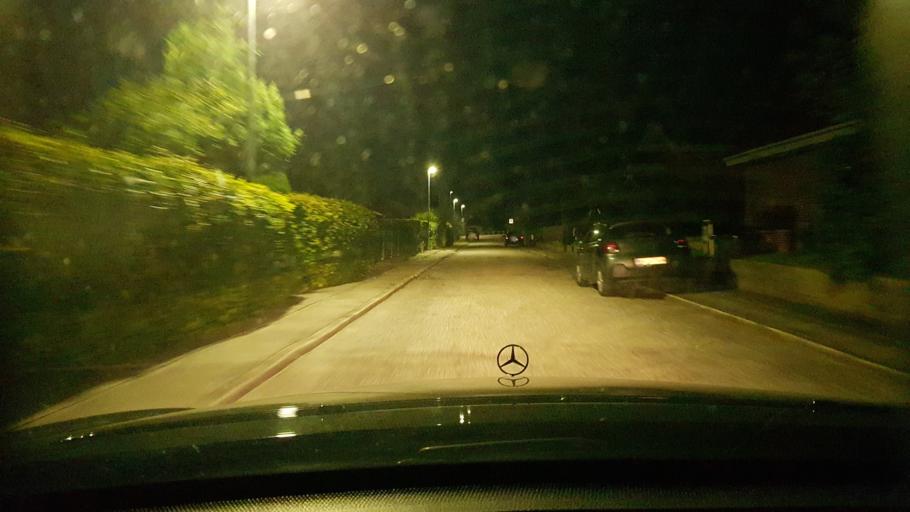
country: DK
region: North Denmark
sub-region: Mariagerfjord Kommune
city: Hadsund
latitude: 56.7225
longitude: 10.1191
